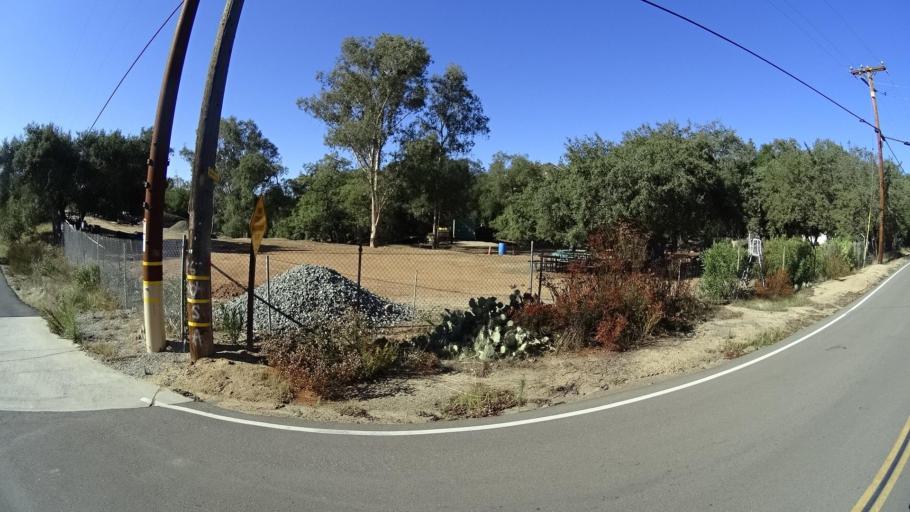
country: MX
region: Baja California
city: Tecate
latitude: 32.6730
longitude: -116.7080
